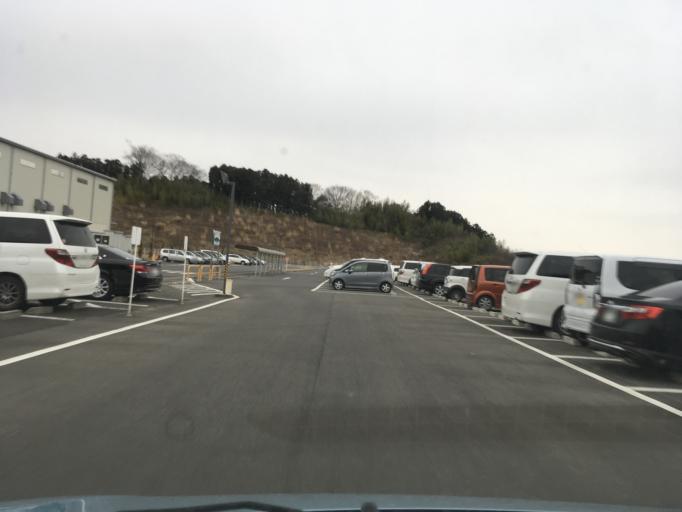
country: JP
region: Miyagi
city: Wakuya
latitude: 38.6998
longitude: 141.1663
